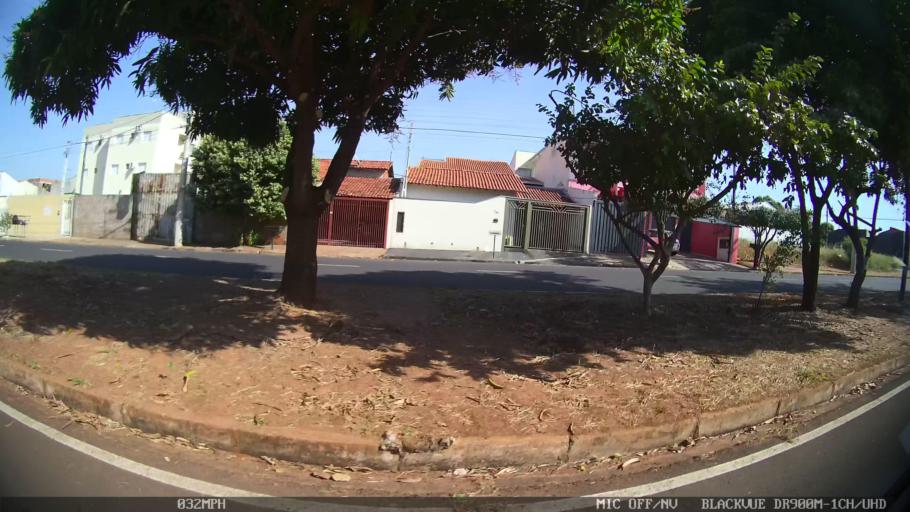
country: BR
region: Sao Paulo
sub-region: Sao Jose Do Rio Preto
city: Sao Jose do Rio Preto
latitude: -20.7911
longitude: -49.4356
